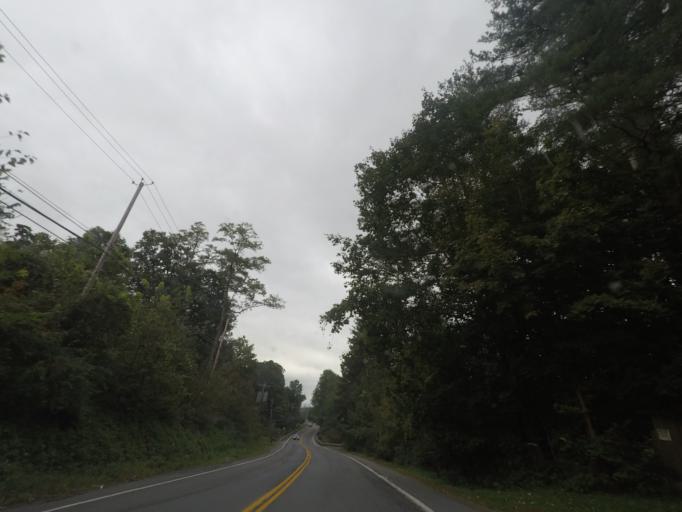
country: US
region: New York
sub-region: Rensselaer County
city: Hoosick Falls
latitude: 42.9115
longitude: -73.3521
